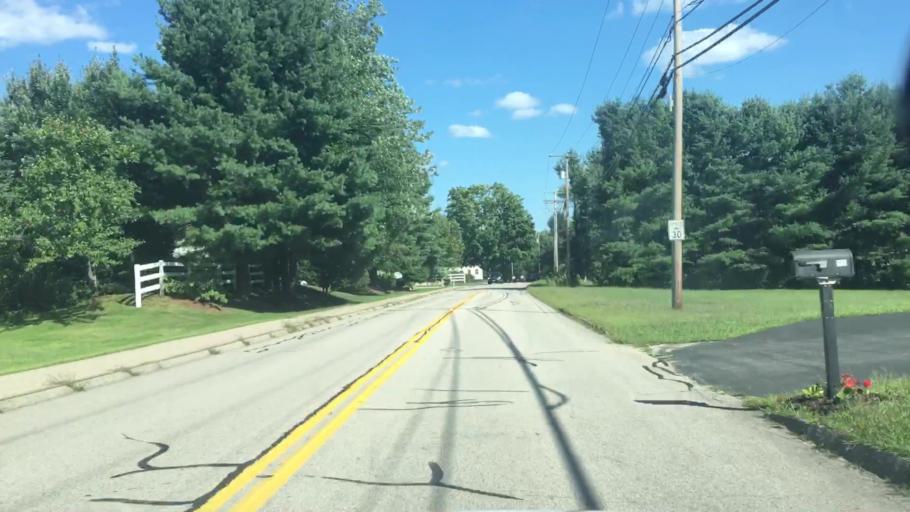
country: US
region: New Hampshire
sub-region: Strafford County
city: Madbury
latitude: 43.1676
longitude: -70.8900
